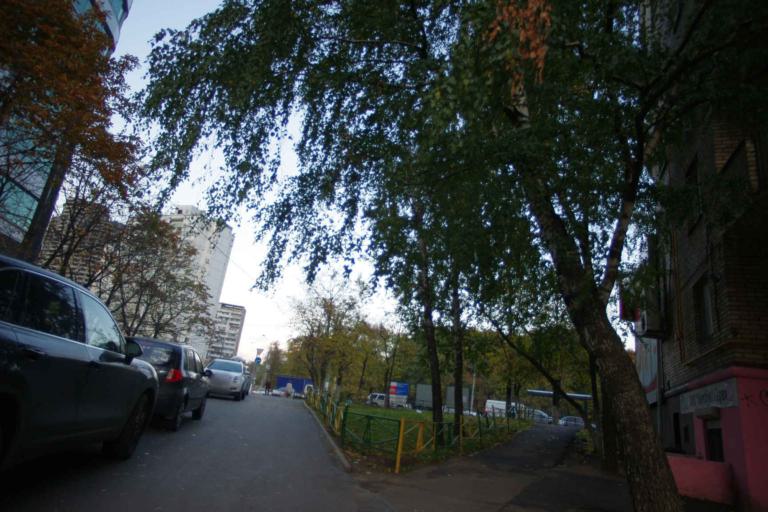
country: RU
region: Moskovskaya
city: Leninskiye Gory
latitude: 55.6925
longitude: 37.5747
